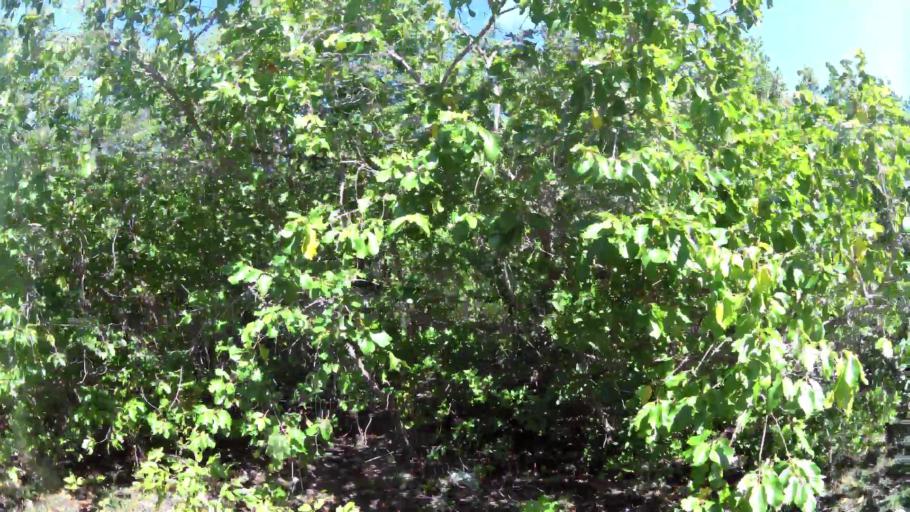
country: AG
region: Barbuda
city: Codrington
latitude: 17.5945
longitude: -61.8284
